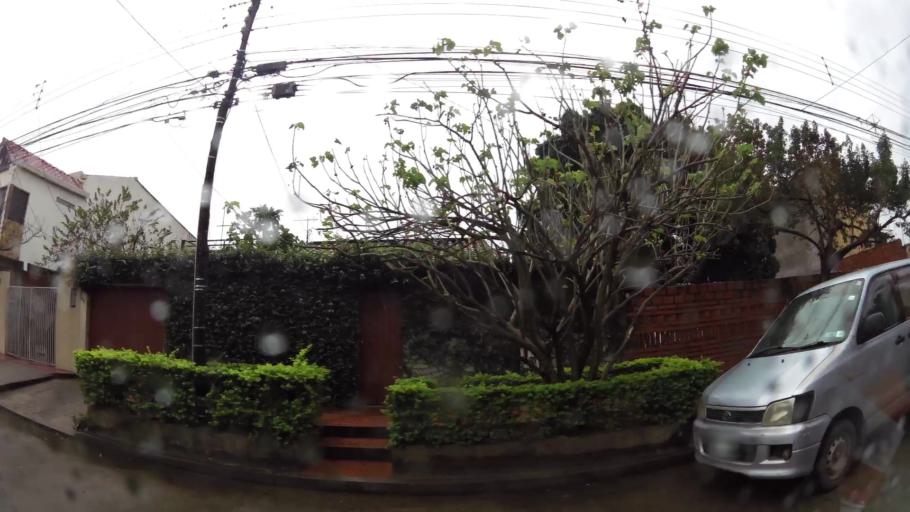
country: BO
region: Santa Cruz
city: Santa Cruz de la Sierra
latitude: -17.7694
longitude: -63.1496
